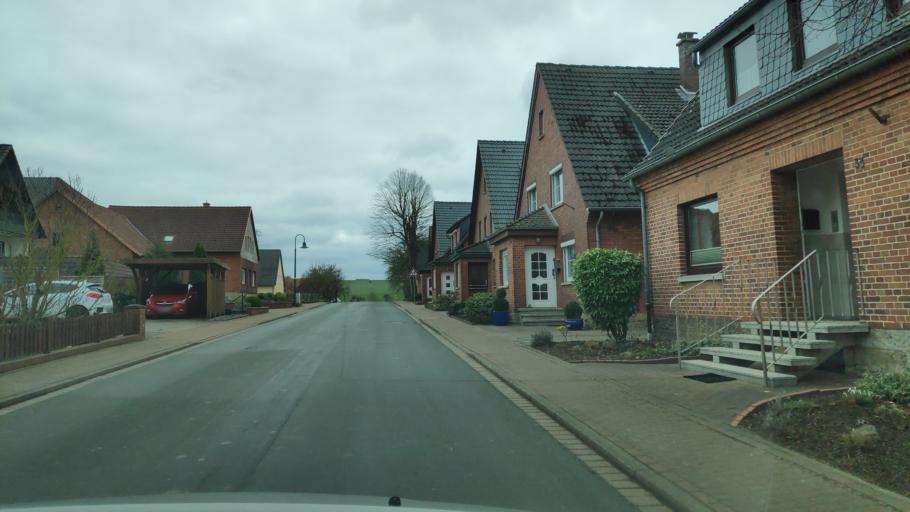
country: DE
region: Lower Saxony
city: Rehren
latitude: 52.2325
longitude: 9.2797
